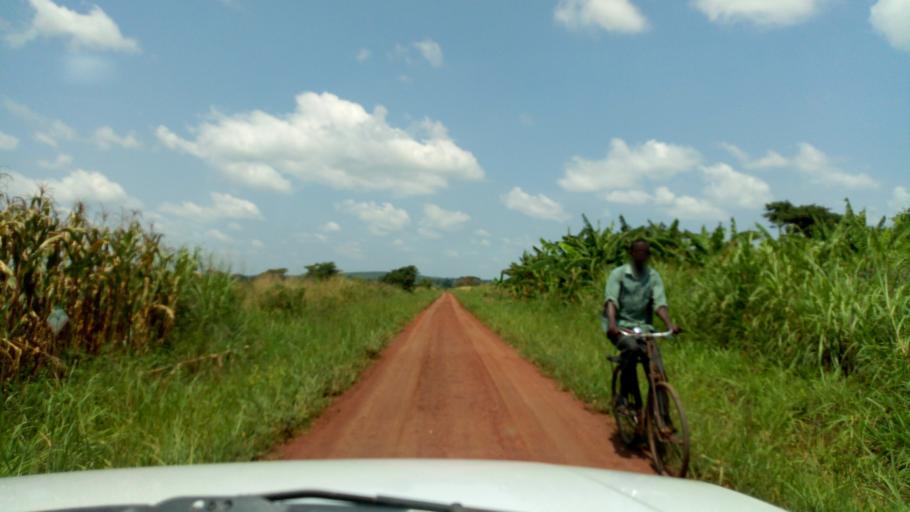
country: UG
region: Western Region
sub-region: Masindi District
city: Masindi
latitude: 1.7517
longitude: 31.8678
